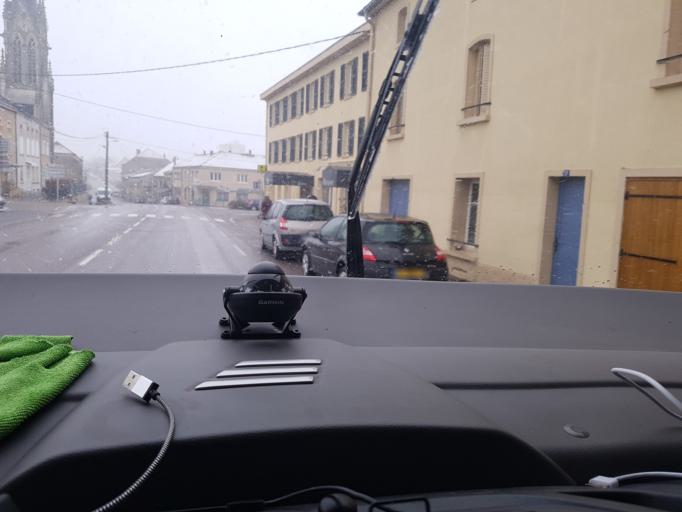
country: FR
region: Lorraine
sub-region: Departement de la Moselle
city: Solgne
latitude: 48.8872
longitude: 6.3919
